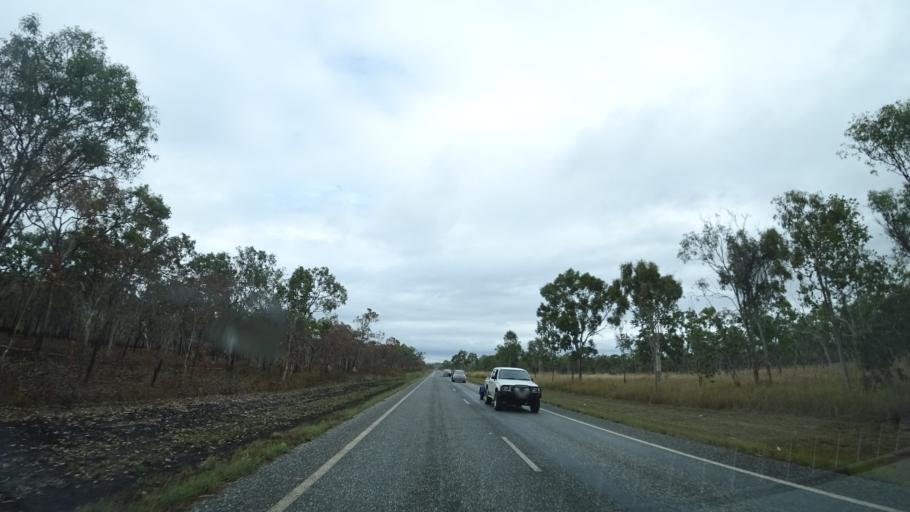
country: AU
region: Queensland
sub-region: Tablelands
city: Mareeba
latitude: -16.7543
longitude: 145.3428
